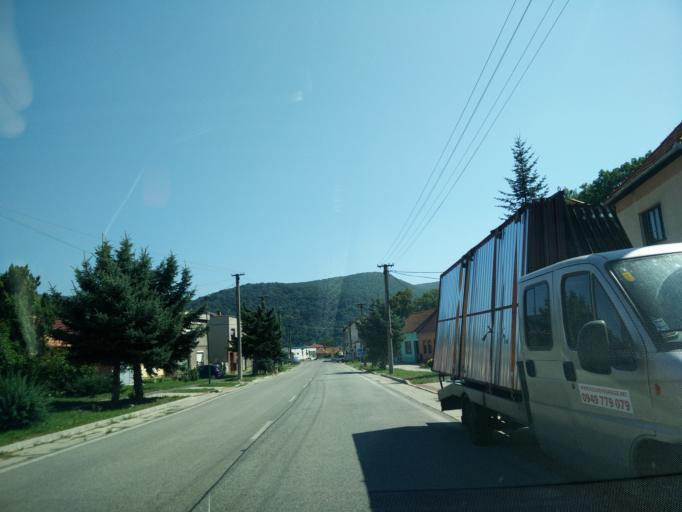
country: SK
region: Nitriansky
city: Tlmace
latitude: 48.3461
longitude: 18.5567
